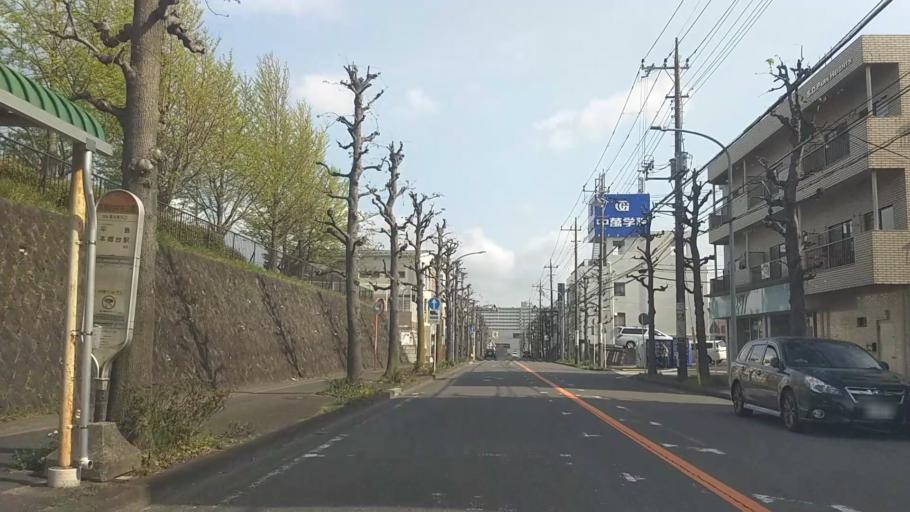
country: JP
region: Kanagawa
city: Kamakura
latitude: 35.3718
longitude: 139.5463
